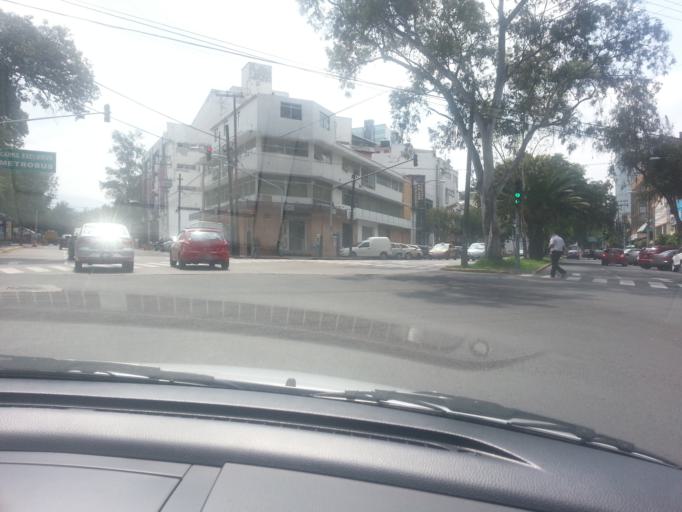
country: MX
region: Mexico City
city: Alvaro Obregon
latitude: 19.3482
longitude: -99.1846
